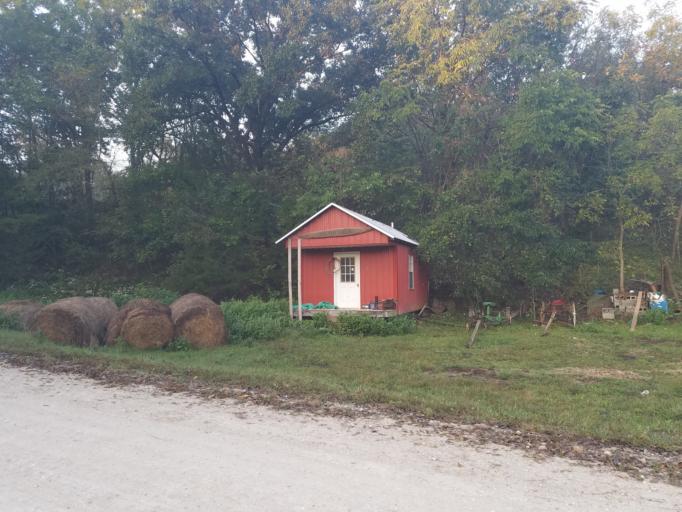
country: US
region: Missouri
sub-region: Moniteau County
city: California
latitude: 38.7440
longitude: -92.6281
